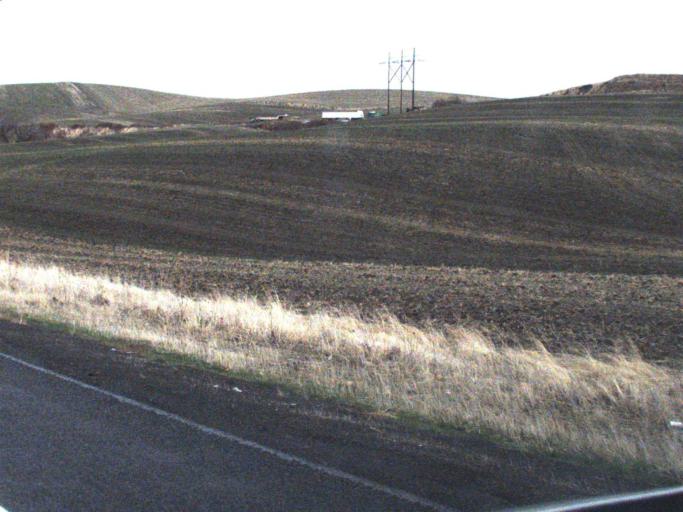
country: US
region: Washington
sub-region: Walla Walla County
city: Waitsburg
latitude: 46.1715
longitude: -118.1334
